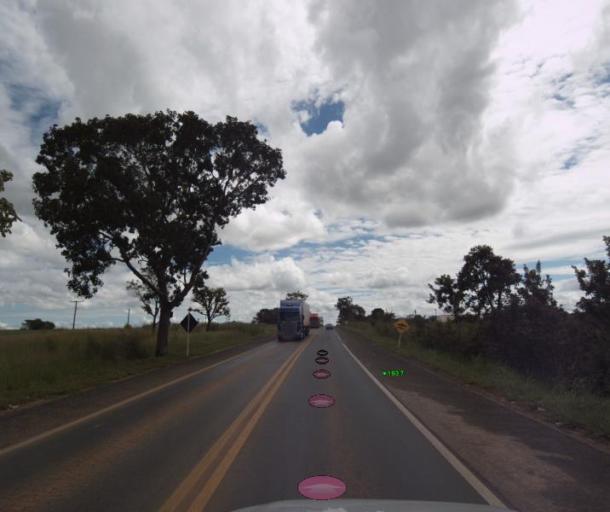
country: BR
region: Goias
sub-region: Uruacu
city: Uruacu
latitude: -14.4728
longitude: -49.1559
